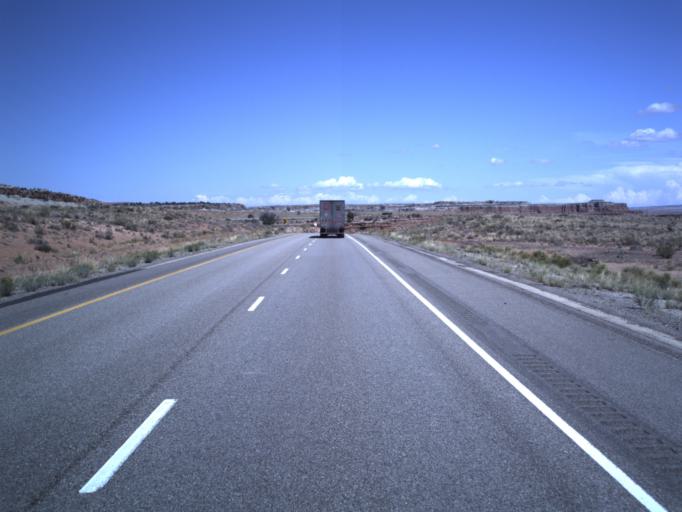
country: US
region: Utah
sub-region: Emery County
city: Ferron
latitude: 38.8347
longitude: -111.1033
